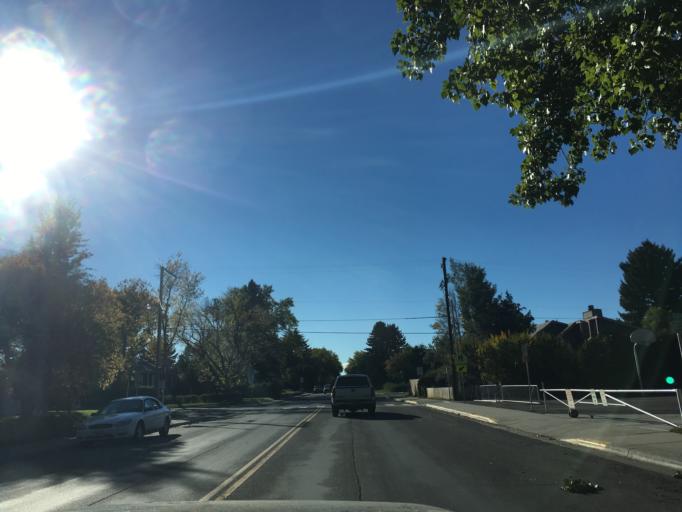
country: US
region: Montana
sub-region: Yellowstone County
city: Billings
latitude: 45.7899
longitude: -108.5350
